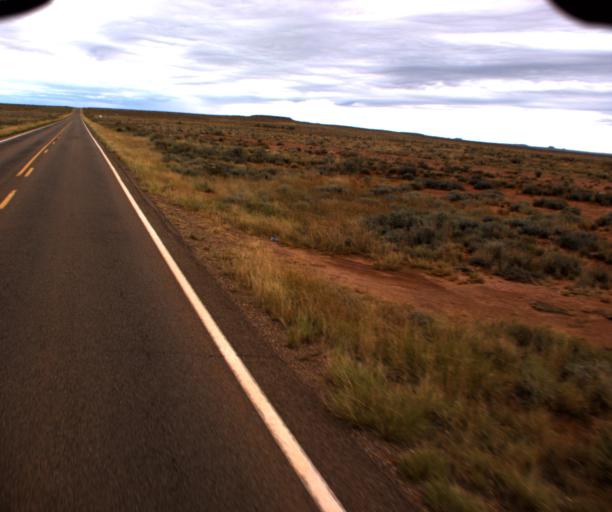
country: US
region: Arizona
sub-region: Navajo County
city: Holbrook
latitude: 34.7606
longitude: -110.1247
